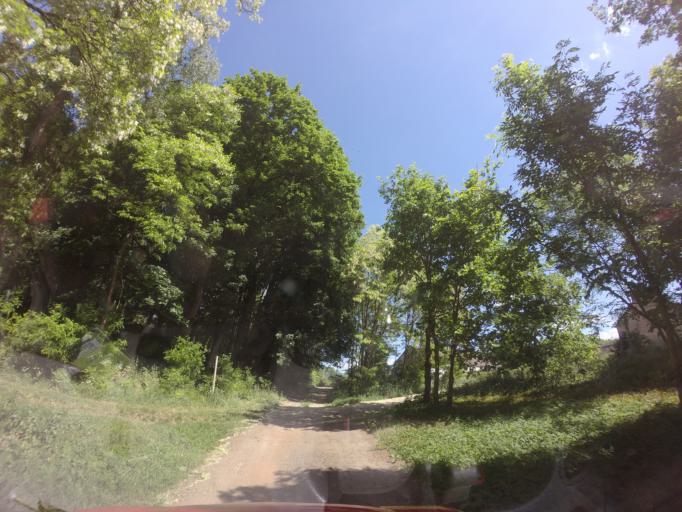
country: PL
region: West Pomeranian Voivodeship
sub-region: Powiat choszczenski
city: Recz
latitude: 53.2484
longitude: 15.5418
